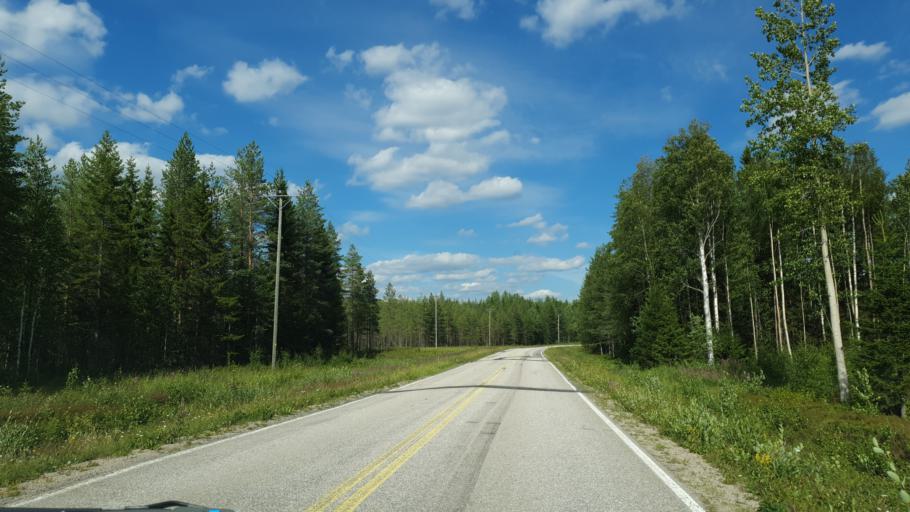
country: FI
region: Kainuu
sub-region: Kajaani
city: Sotkamo
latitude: 64.1989
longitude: 28.9043
